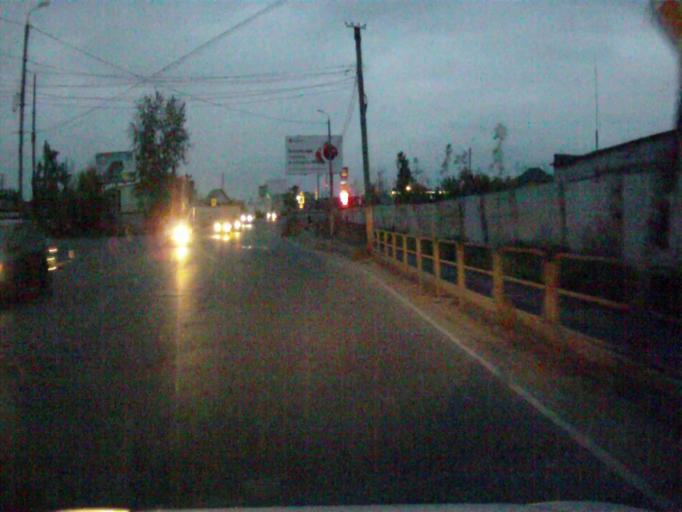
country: RU
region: Chelyabinsk
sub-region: Gorod Chelyabinsk
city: Chelyabinsk
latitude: 55.1535
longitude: 61.3030
